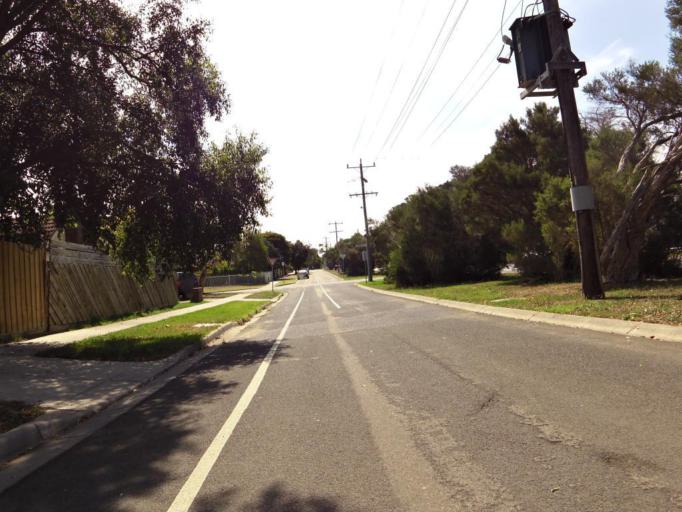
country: AU
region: Victoria
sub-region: Mornington Peninsula
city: Tyabb
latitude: -38.2326
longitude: 145.1836
